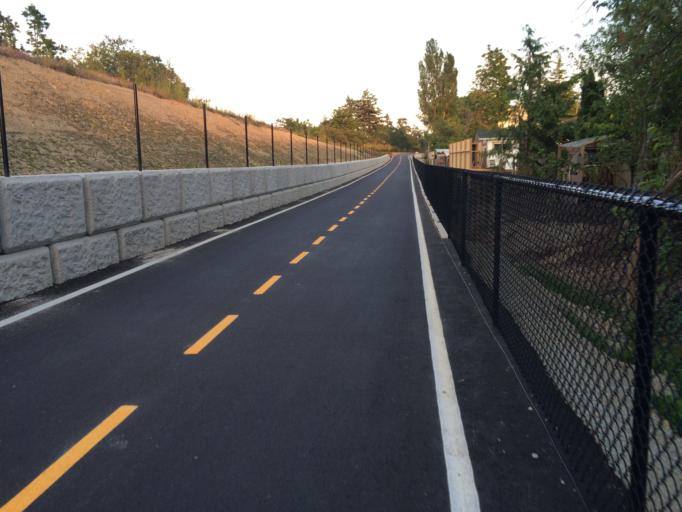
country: CA
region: British Columbia
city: Colwood
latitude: 48.4561
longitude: -123.4331
